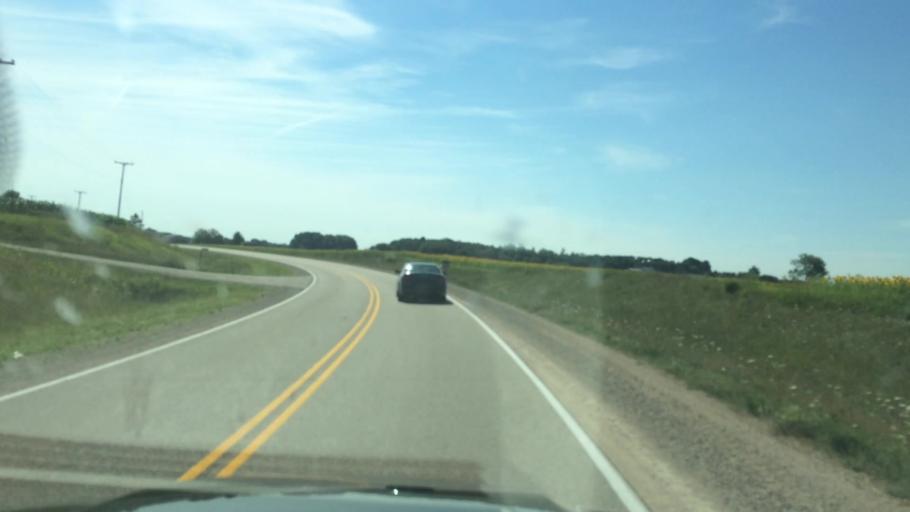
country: US
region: Wisconsin
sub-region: Shawano County
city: Bonduel
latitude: 44.7878
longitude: -88.3511
